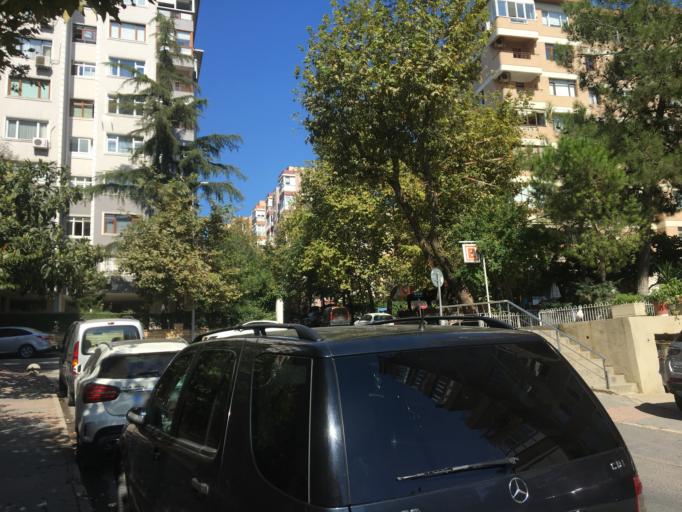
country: TR
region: Istanbul
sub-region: Atasehir
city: Atasehir
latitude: 40.9609
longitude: 29.1038
